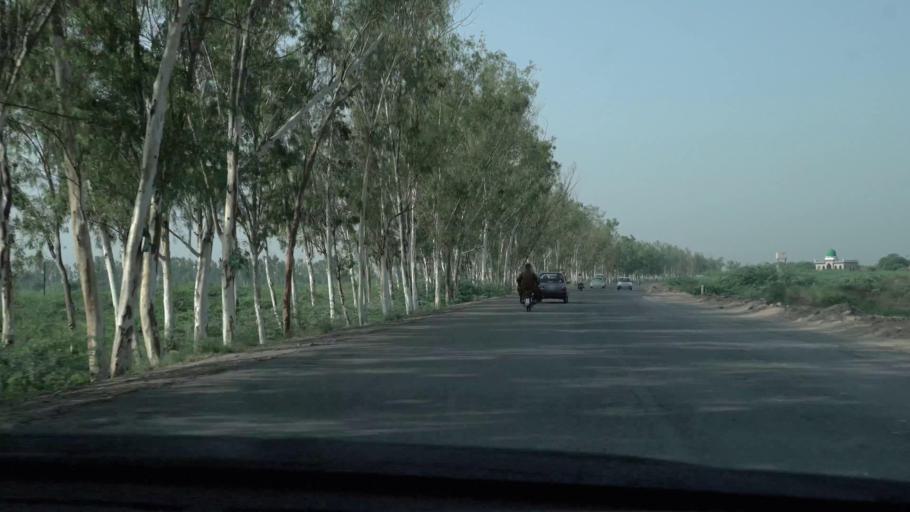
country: PK
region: Punjab
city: Gojra
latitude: 31.1138
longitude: 72.6651
